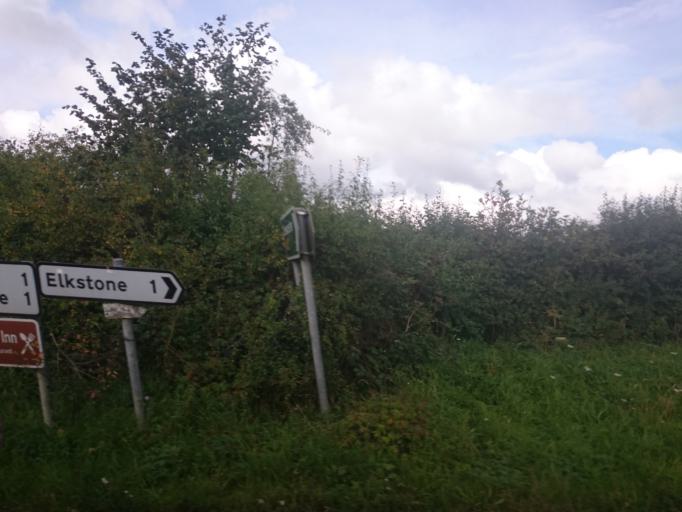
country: GB
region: England
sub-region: Gloucestershire
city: Charlton Kings
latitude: 51.7978
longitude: -2.0501
